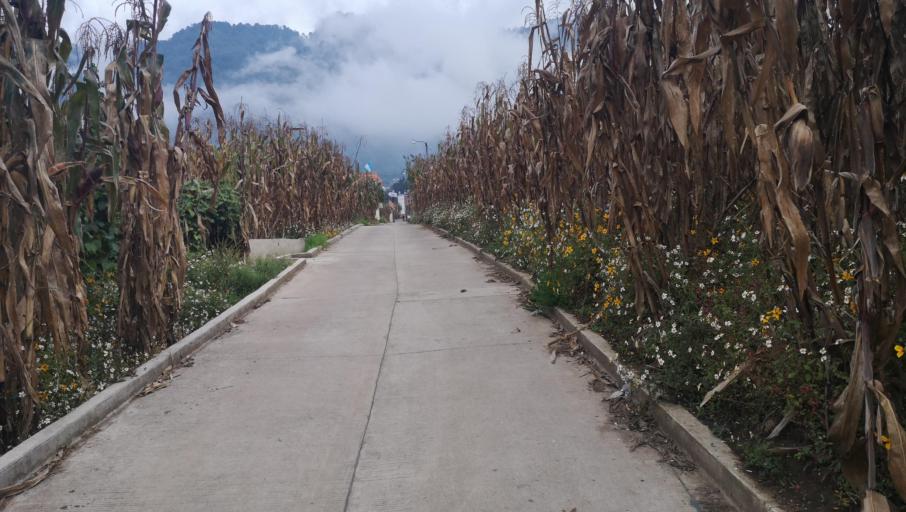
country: GT
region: Quetzaltenango
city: Cantel
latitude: 14.8184
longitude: -91.4367
